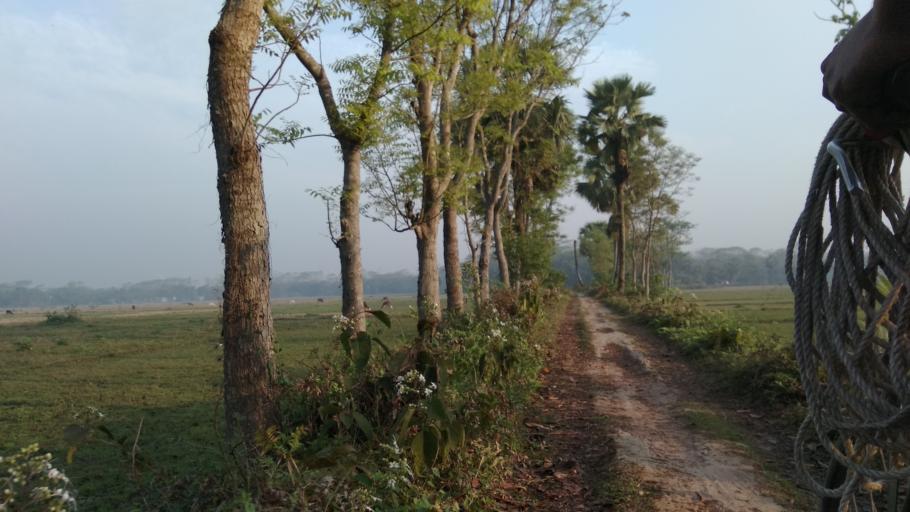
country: BD
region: Barisal
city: Mehendiganj
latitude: 22.9336
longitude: 90.4137
